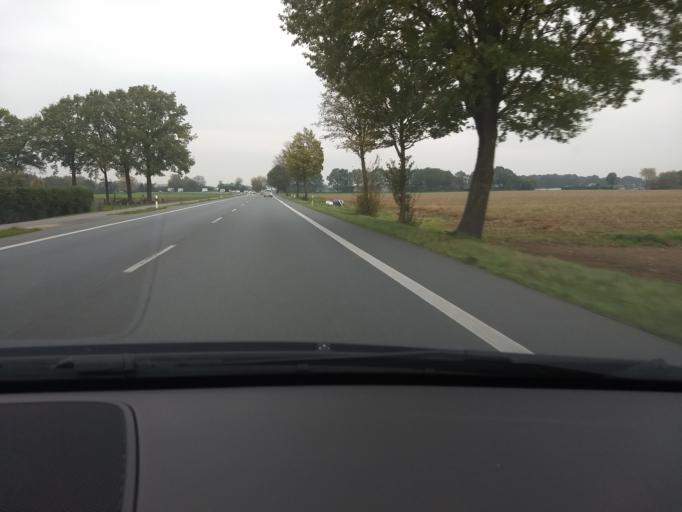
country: DE
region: North Rhine-Westphalia
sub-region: Regierungsbezirk Munster
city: Raesfeld
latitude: 51.7566
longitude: 6.8607
